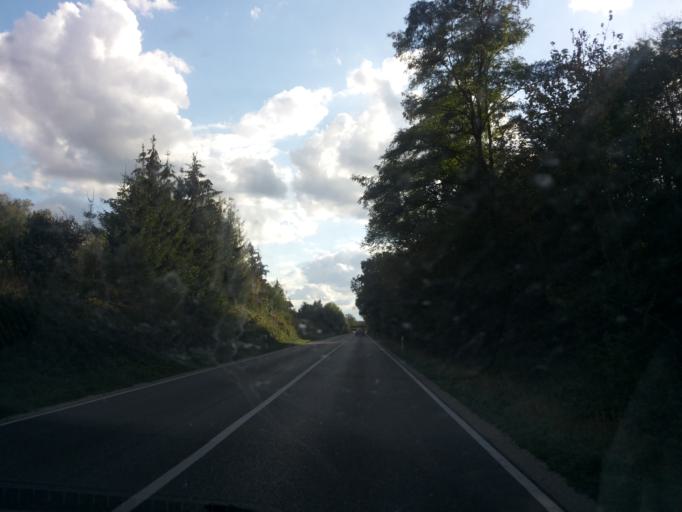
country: DE
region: Bavaria
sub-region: Upper Bavaria
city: Gaimersheim
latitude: 48.7845
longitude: 11.3673
